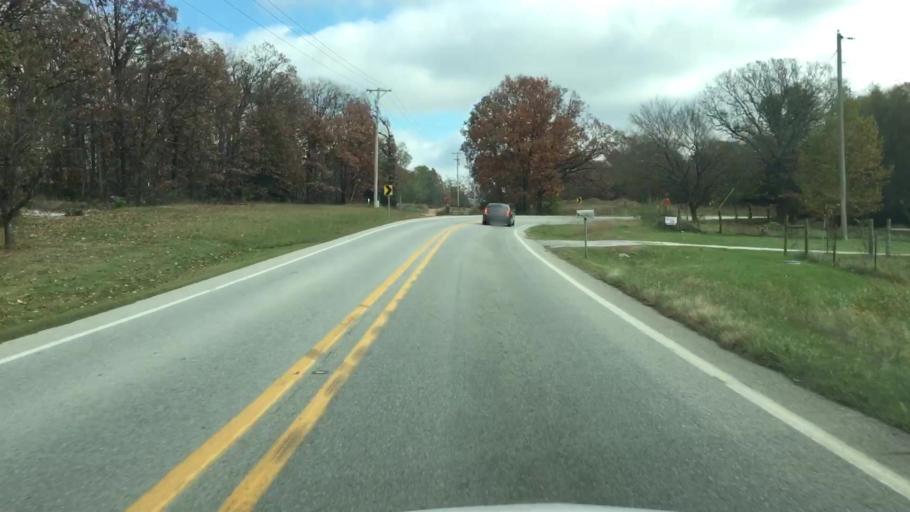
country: US
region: Arkansas
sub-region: Benton County
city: Gentry
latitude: 36.2633
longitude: -94.4529
